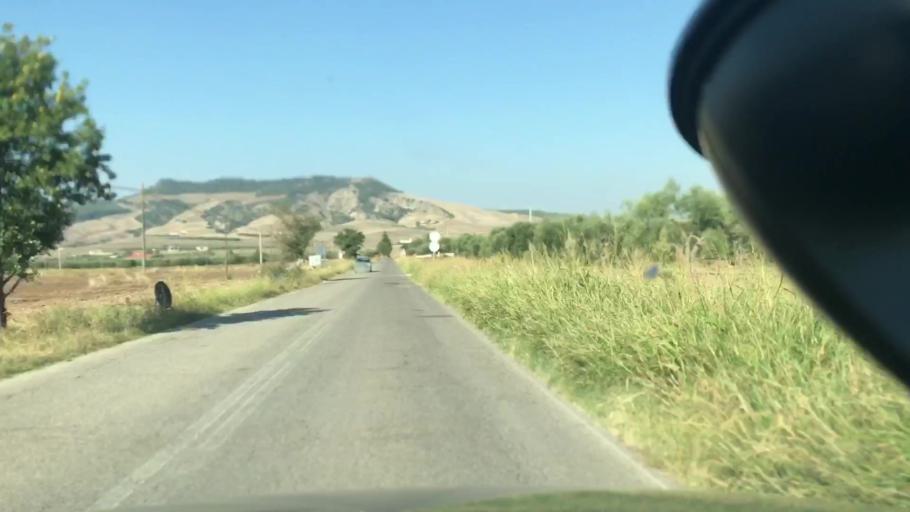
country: IT
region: Basilicate
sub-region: Provincia di Matera
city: La Martella
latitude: 40.6583
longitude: 16.5298
